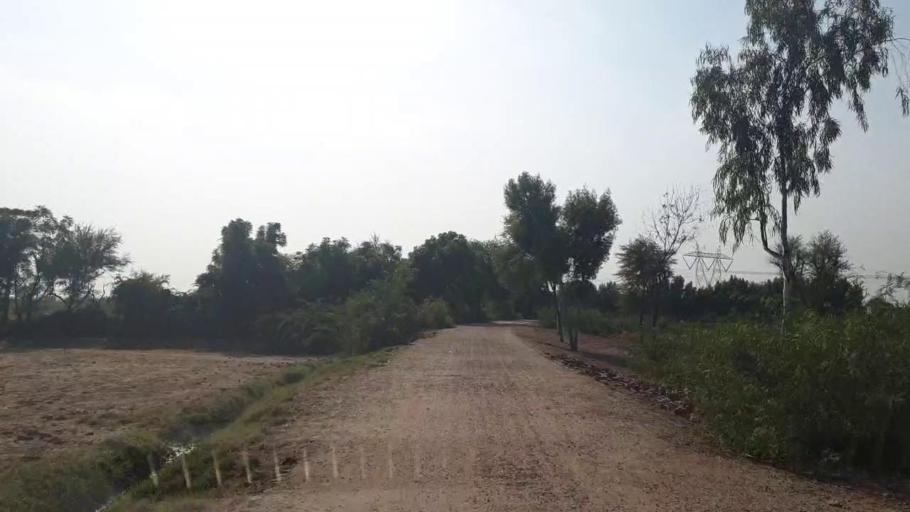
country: PK
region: Sindh
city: Hyderabad
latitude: 25.4679
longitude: 68.3785
